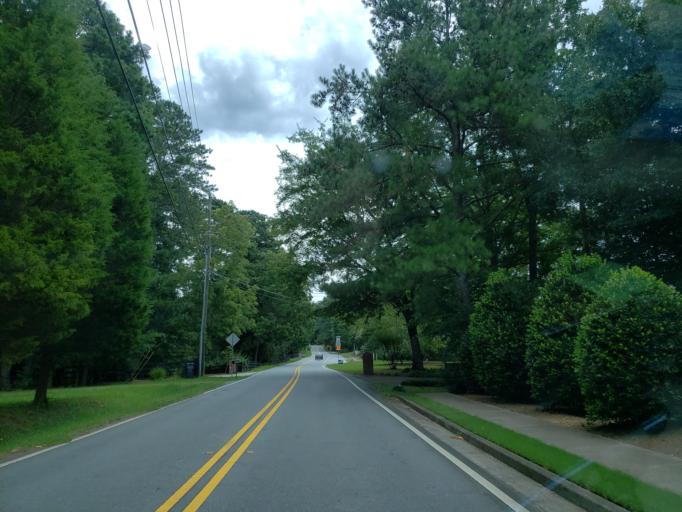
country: US
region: Georgia
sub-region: Cobb County
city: Acworth
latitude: 34.0185
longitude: -84.6935
